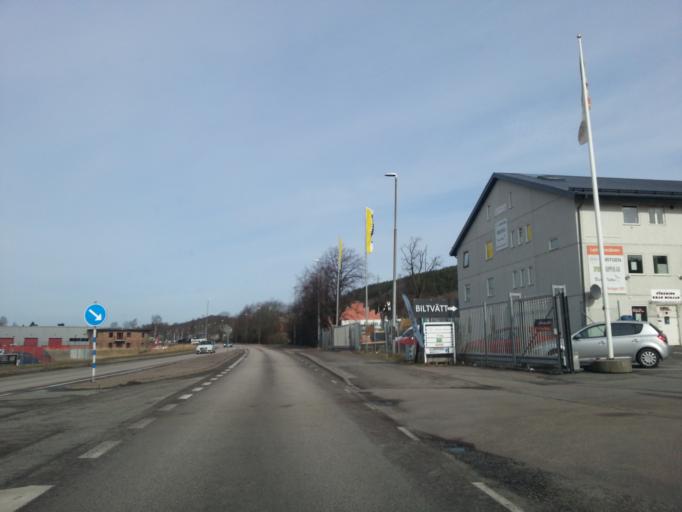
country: SE
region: Vaestra Goetaland
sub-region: Goteborg
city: Eriksbo
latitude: 57.7494
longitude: 12.0107
